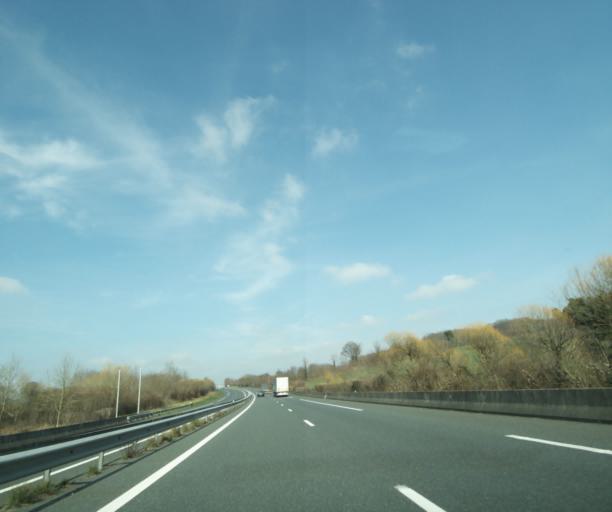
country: FR
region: Limousin
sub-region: Departement de la Haute-Vienne
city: Saint-Sulpice-les-Feuilles
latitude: 46.3797
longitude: 1.4474
